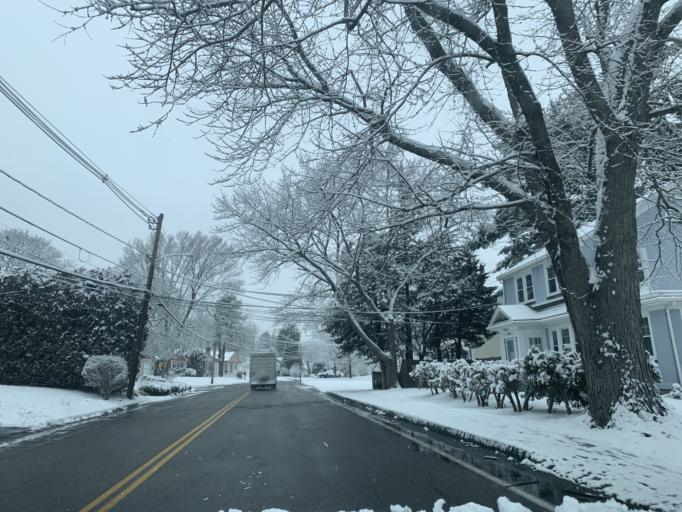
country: US
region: Massachusetts
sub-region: Norfolk County
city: Norwood
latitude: 42.2003
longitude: -71.1898
